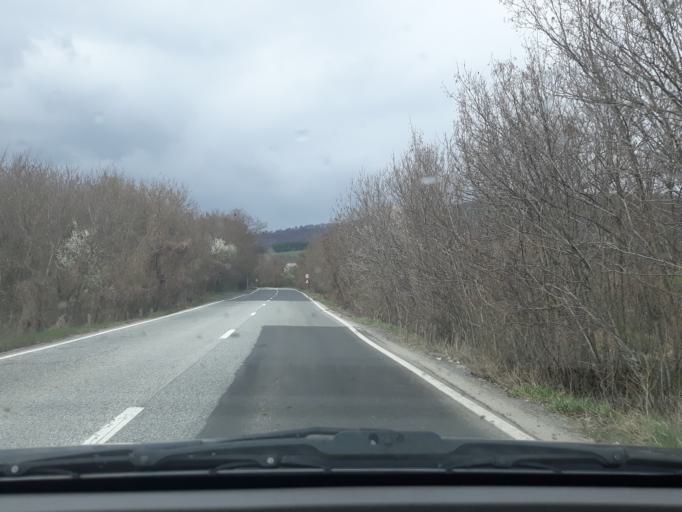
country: RO
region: Harghita
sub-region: Comuna Lupeni
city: Lupeni
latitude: 46.4019
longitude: 25.2157
